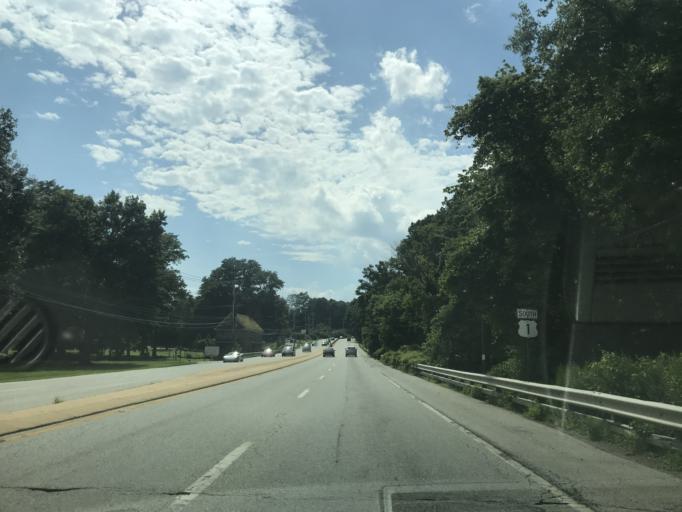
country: US
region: Pennsylvania
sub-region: Chester County
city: West Chester
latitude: 39.8741
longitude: -75.6242
